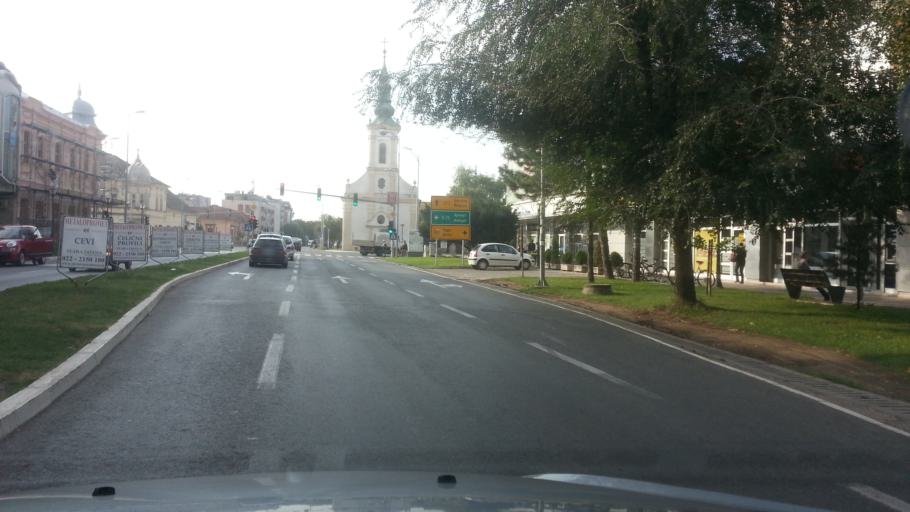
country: RS
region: Autonomna Pokrajina Vojvodina
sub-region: Sremski Okrug
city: Stara Pazova
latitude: 44.9855
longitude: 20.1585
